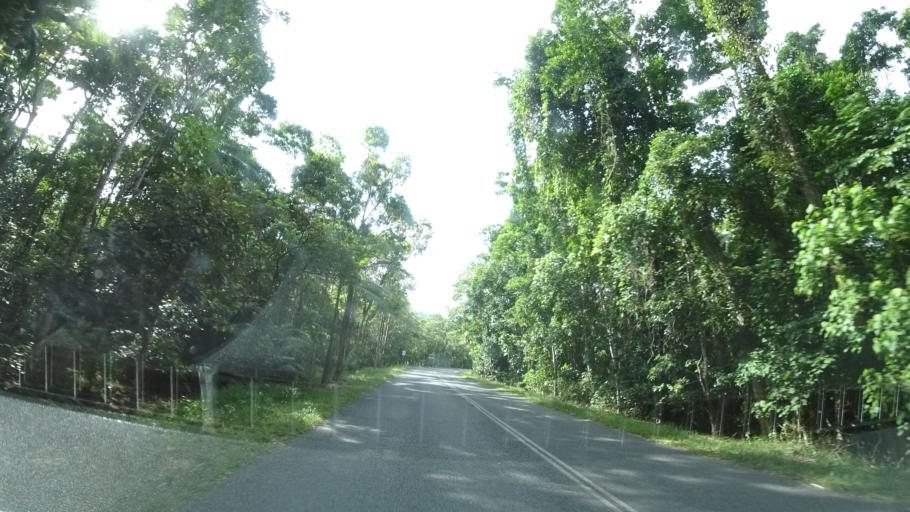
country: AU
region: Queensland
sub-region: Cairns
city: Port Douglas
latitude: -16.0926
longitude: 145.4605
